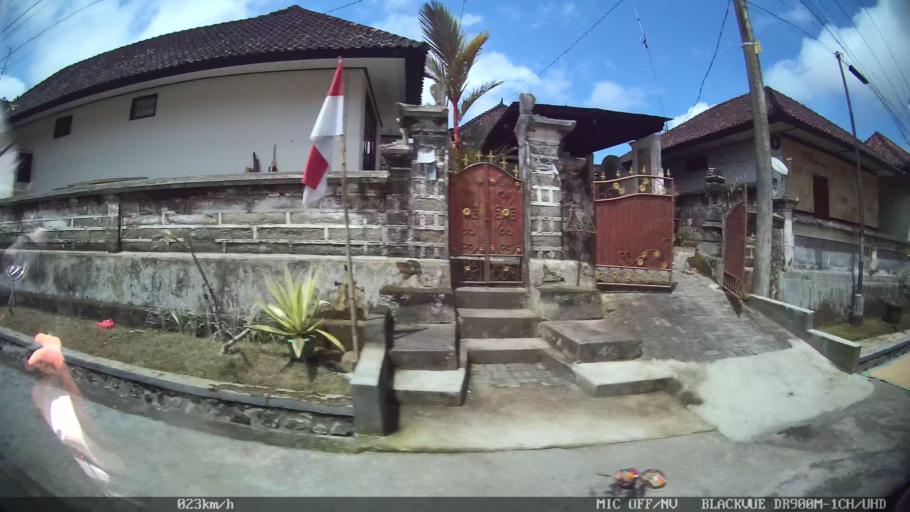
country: ID
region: Bali
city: Banjar Bebalang
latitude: -8.4804
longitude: 115.3430
